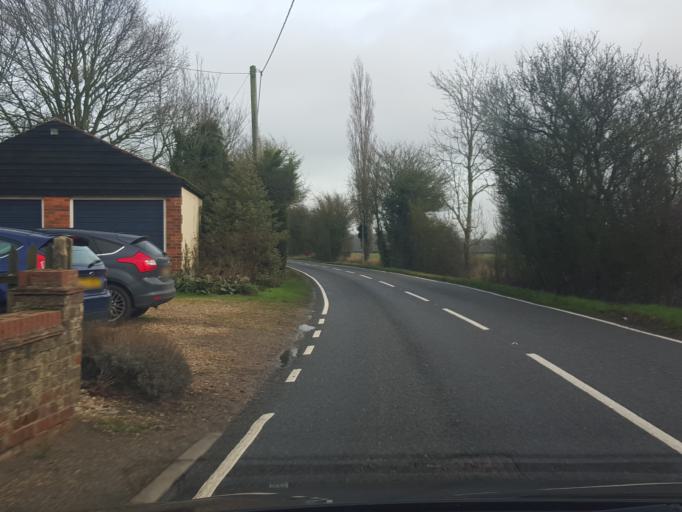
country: GB
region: England
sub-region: Essex
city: West Bergholt
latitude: 51.9488
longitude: 0.8151
